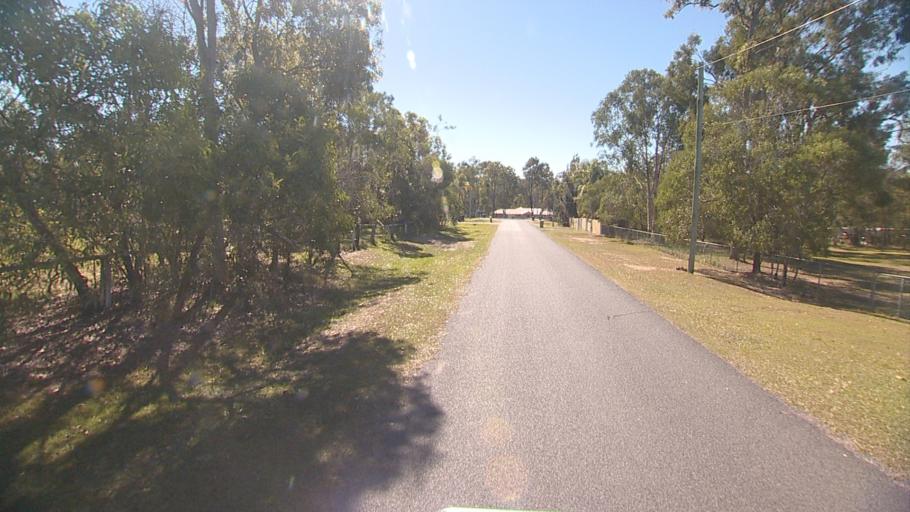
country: AU
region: Queensland
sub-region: Logan
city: Park Ridge South
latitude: -27.7282
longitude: 153.0564
